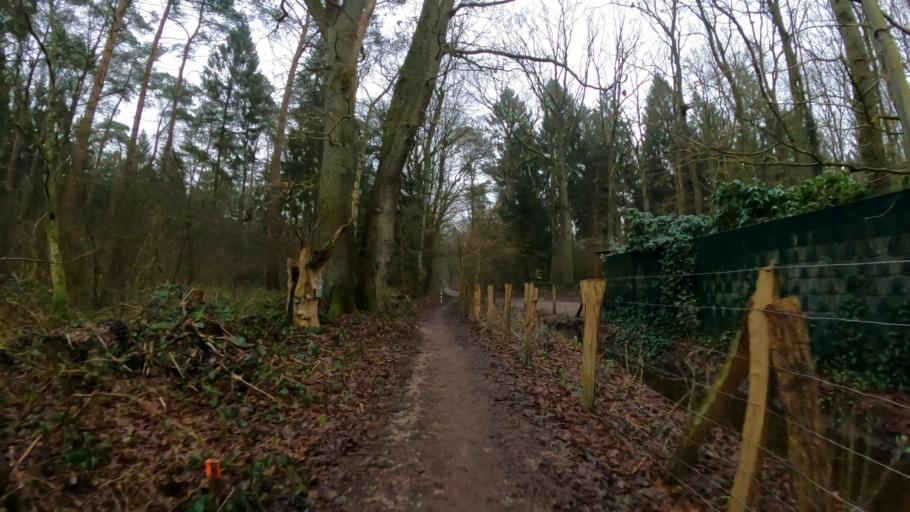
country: DE
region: Schleswig-Holstein
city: Wedel
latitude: 53.5957
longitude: 9.7367
